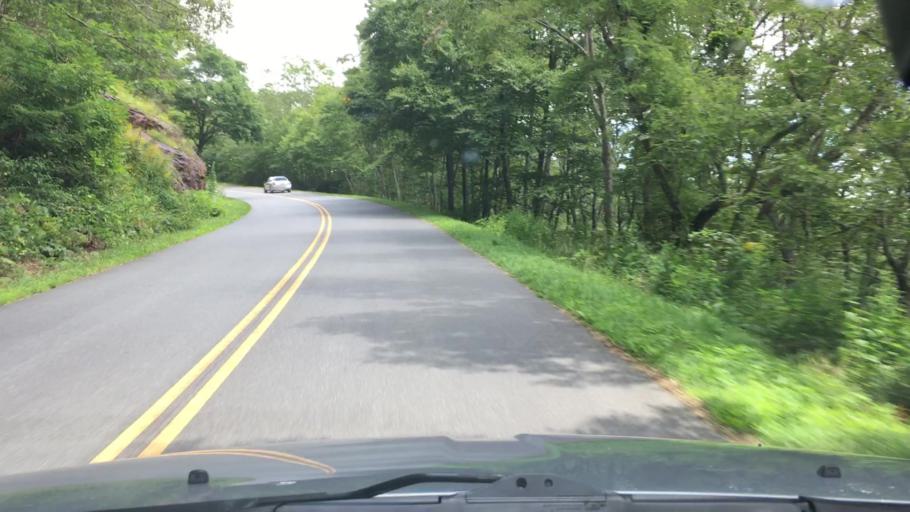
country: US
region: North Carolina
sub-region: Buncombe County
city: Swannanoa
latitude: 35.6753
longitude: -82.4228
